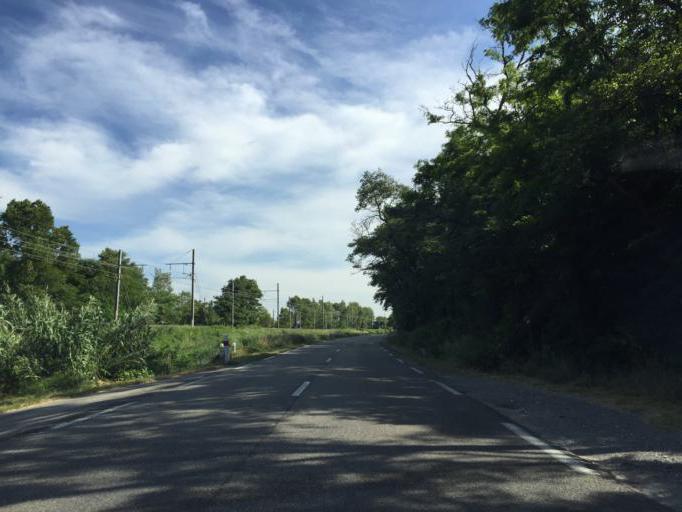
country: FR
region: Rhone-Alpes
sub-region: Departement de l'Ardeche
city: Meysse
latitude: 44.6294
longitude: 4.7432
